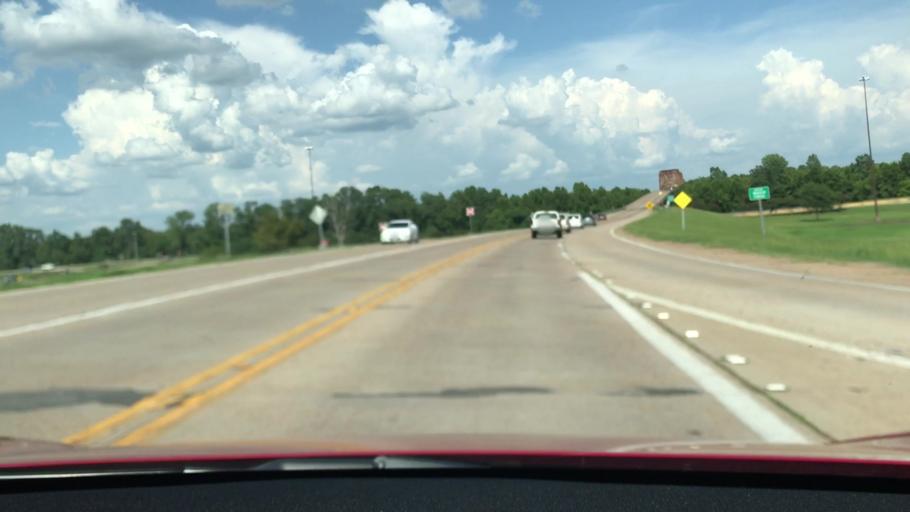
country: US
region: Louisiana
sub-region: Bossier Parish
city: Bossier City
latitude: 32.4587
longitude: -93.6865
